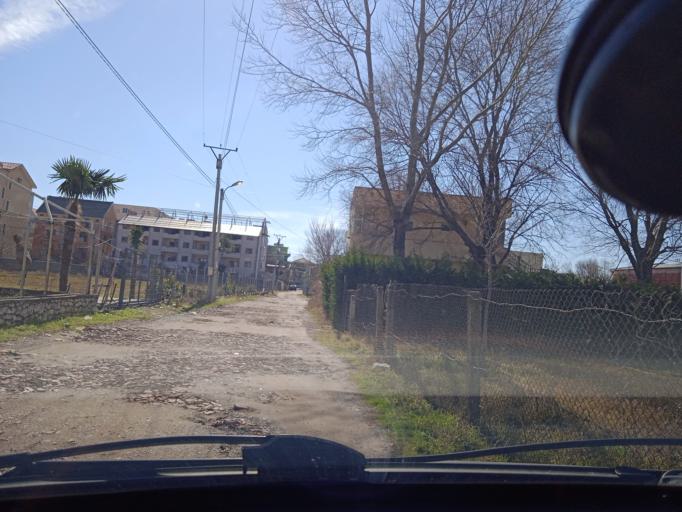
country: AL
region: Shkoder
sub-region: Rrethi i Shkodres
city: Velipoje
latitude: 41.8660
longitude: 19.4214
